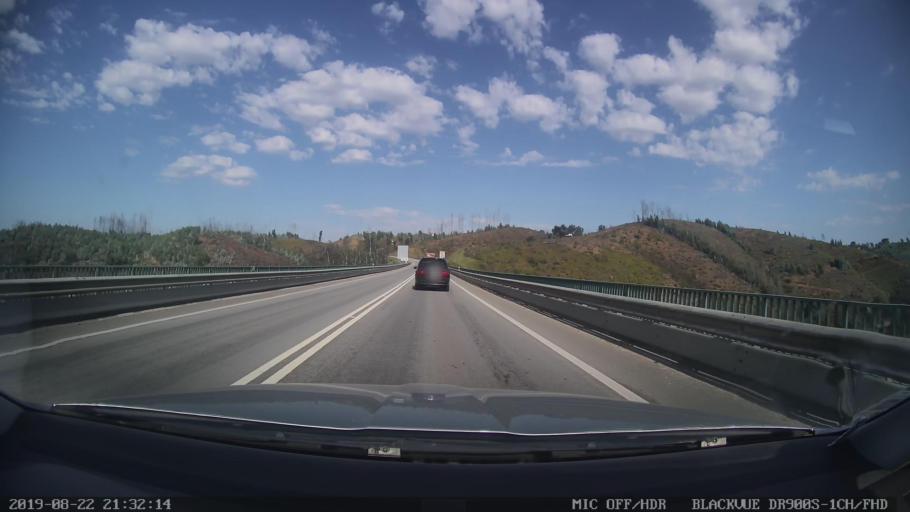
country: PT
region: Leiria
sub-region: Pedrogao Grande
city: Pedrogao Grande
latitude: 39.9261
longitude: -8.1621
